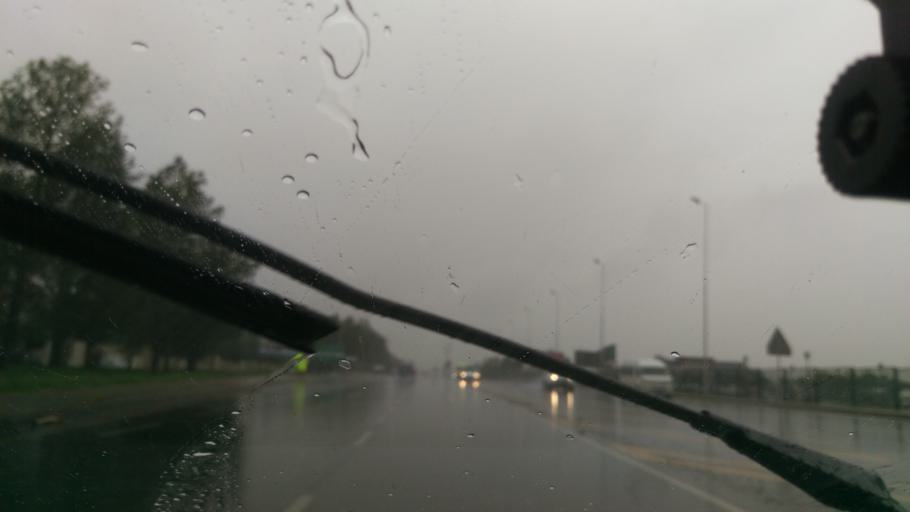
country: ZA
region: Gauteng
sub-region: City of Johannesburg Metropolitan Municipality
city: Diepsloot
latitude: -25.9987
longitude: 27.9835
